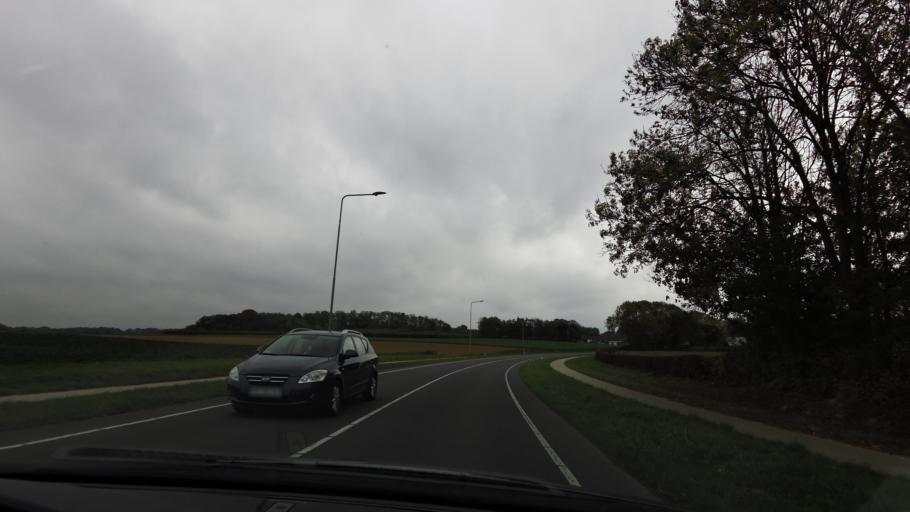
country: NL
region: Limburg
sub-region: Gemeente Schinnen
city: Puth
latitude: 50.9667
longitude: 5.8544
